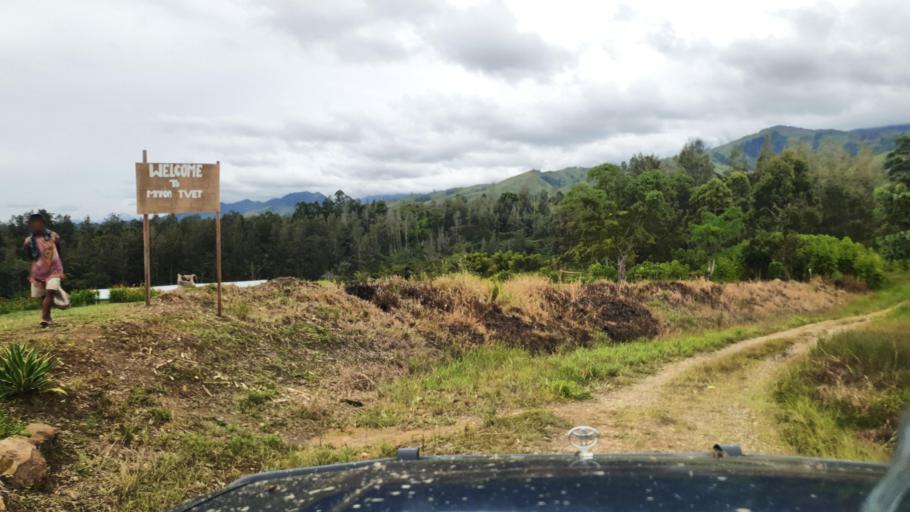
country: PG
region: Jiwaka
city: Minj
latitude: -5.9282
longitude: 144.7481
